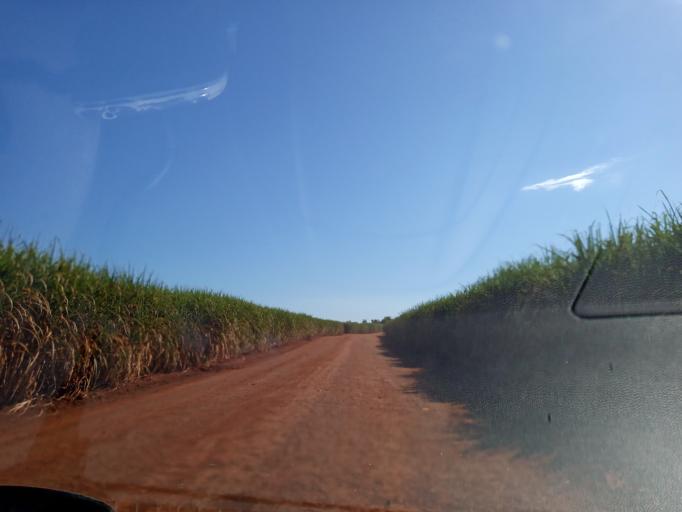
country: BR
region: Goias
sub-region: Itumbiara
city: Itumbiara
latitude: -18.4480
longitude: -49.1778
